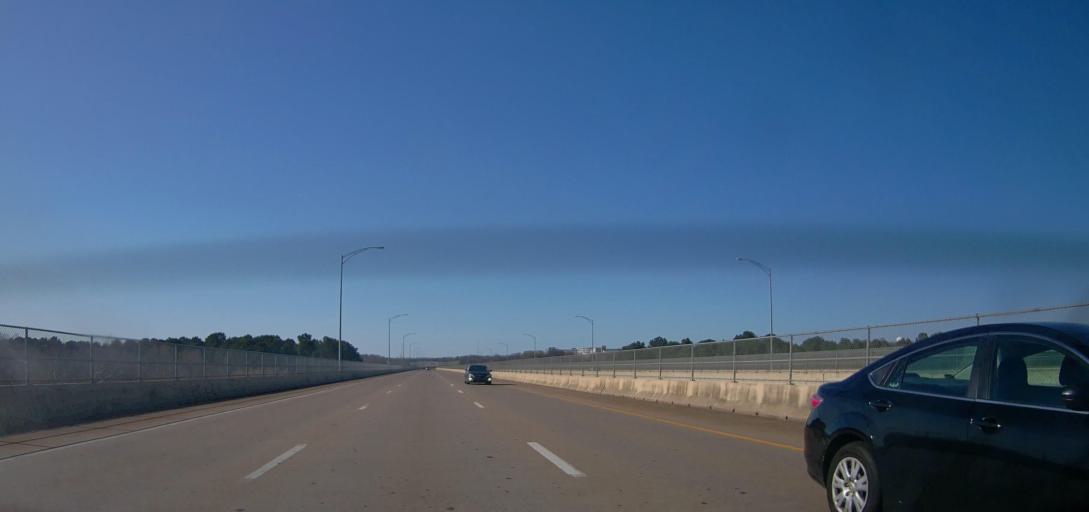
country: US
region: Alabama
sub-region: Lauderdale County
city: East Florence
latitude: 34.7953
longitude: -87.6459
